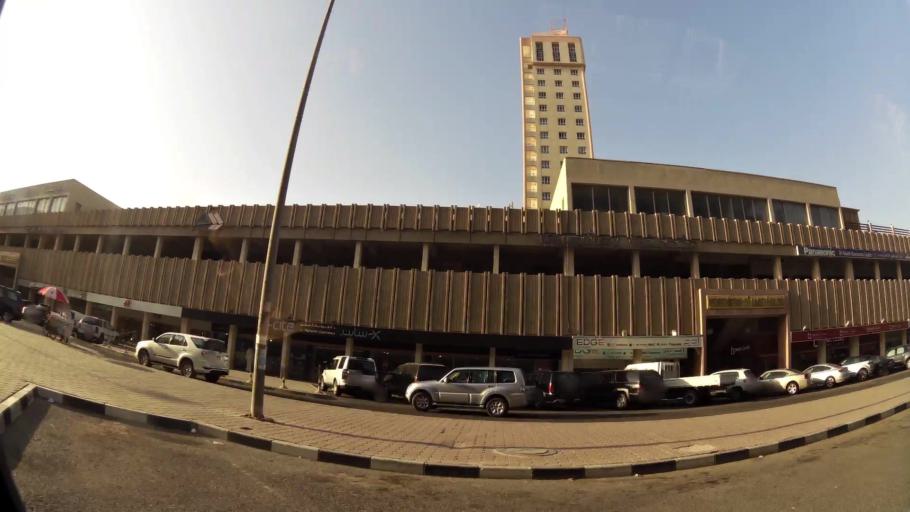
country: KW
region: Muhafazat Hawalli
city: As Salimiyah
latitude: 29.3346
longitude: 48.0614
